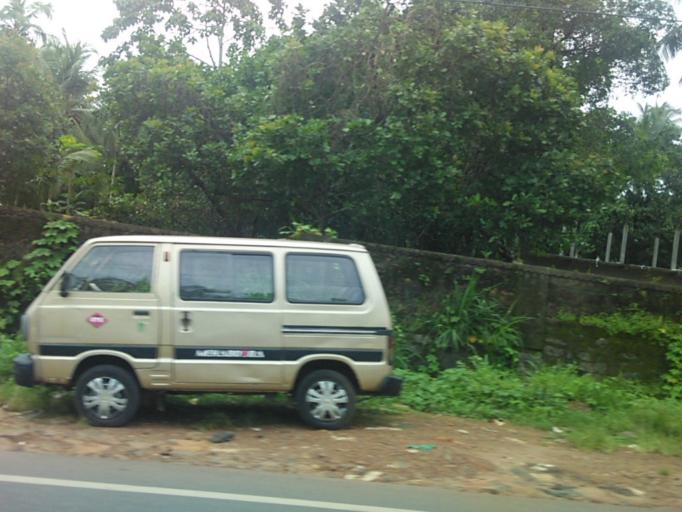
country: IN
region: Kerala
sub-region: Kozhikode
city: Kunnamangalam
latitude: 11.3040
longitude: 75.8676
